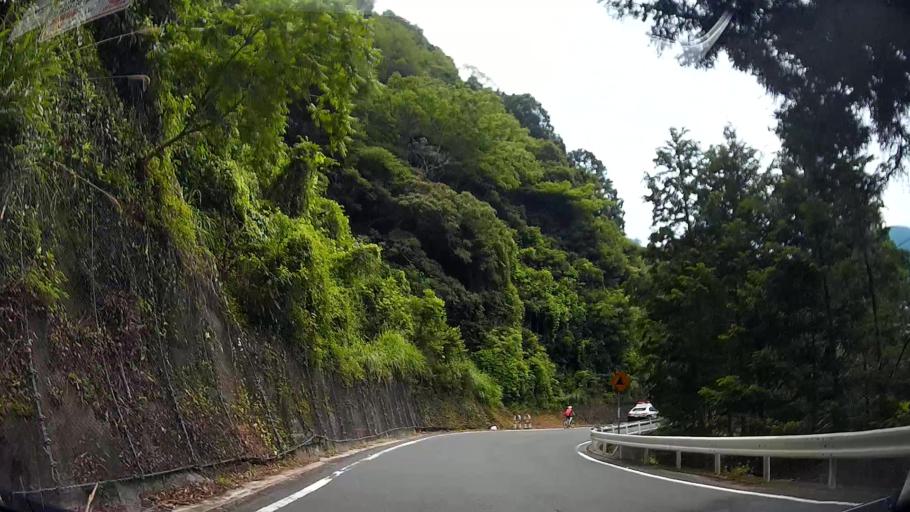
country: JP
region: Shizuoka
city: Mori
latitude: 35.0878
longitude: 137.8355
